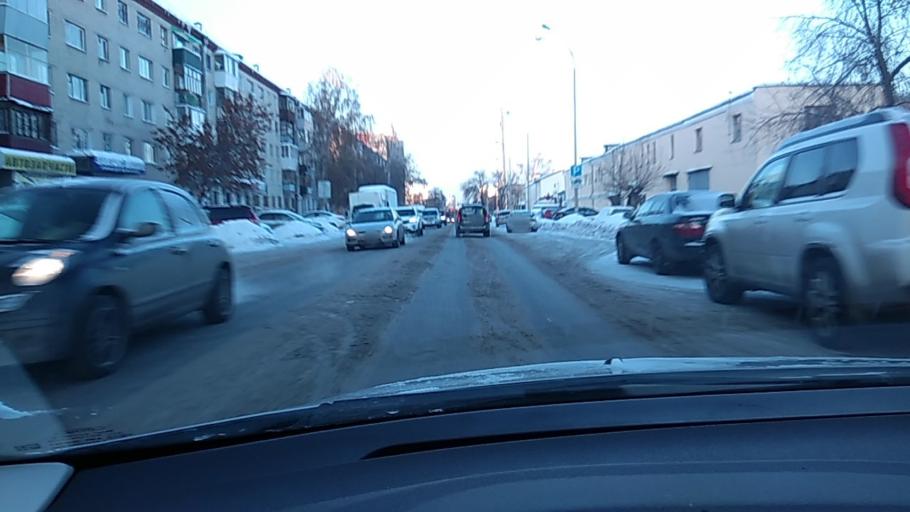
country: RU
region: Sverdlovsk
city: Yekaterinburg
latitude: 56.8110
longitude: 60.6123
